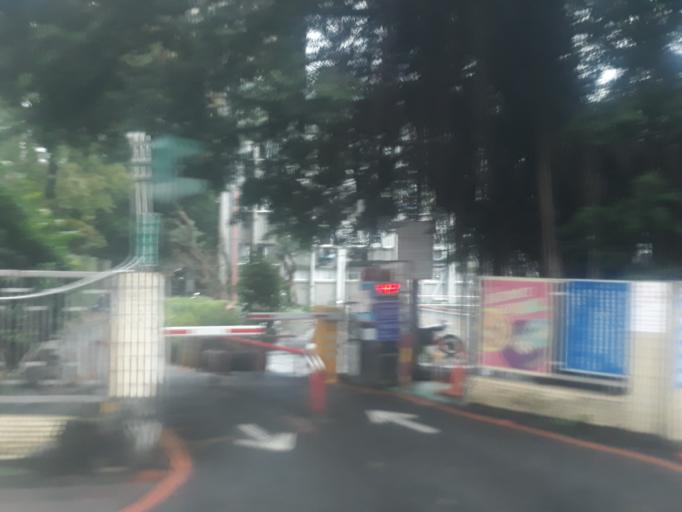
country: TW
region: Taipei
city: Taipei
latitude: 24.9879
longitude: 121.5740
